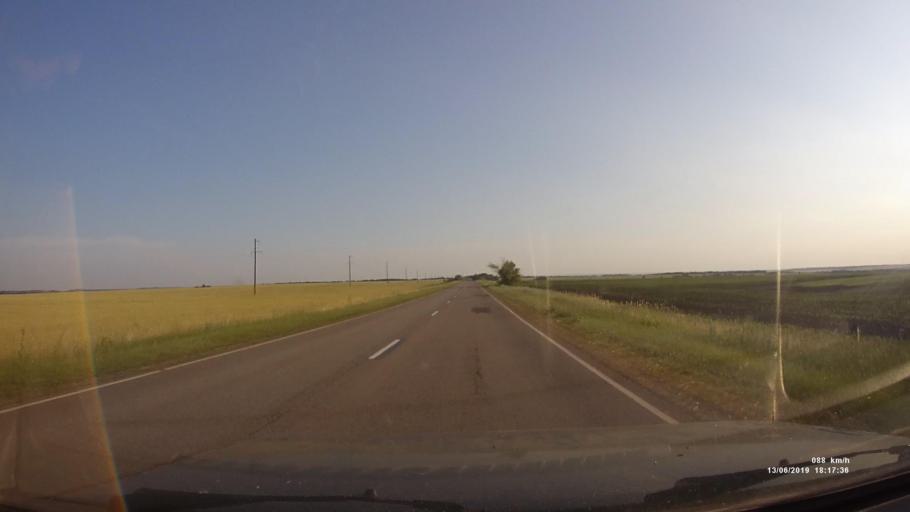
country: RU
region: Rostov
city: Kazanskaya
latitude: 49.9179
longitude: 41.3232
